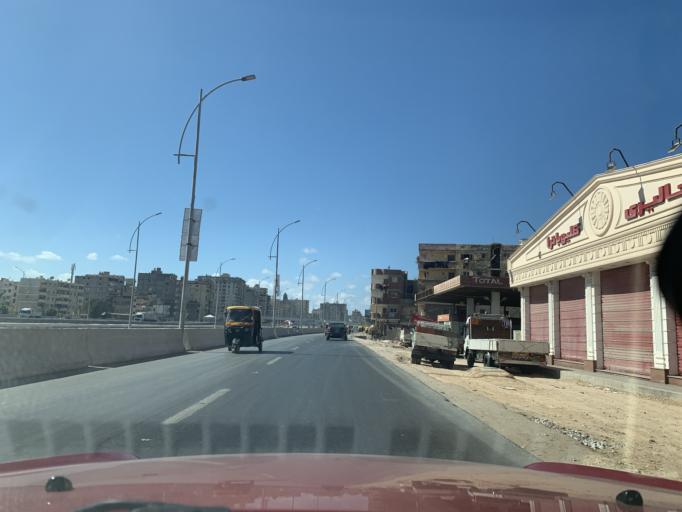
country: EG
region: Alexandria
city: Alexandria
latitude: 31.2176
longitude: 29.9982
